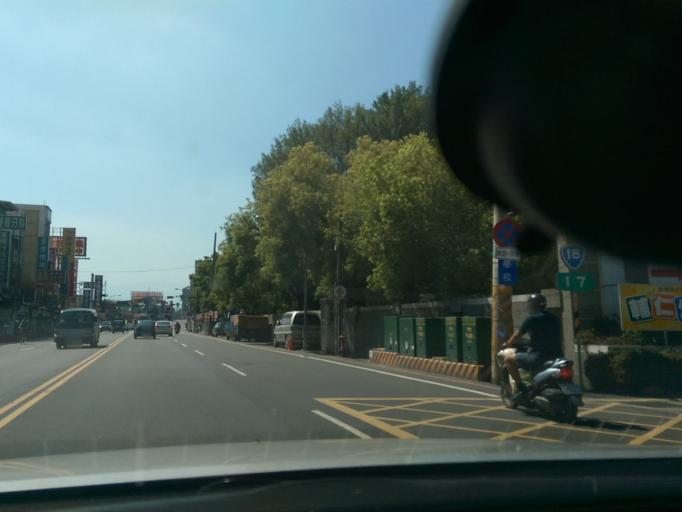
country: TW
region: Taiwan
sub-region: Chiayi
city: Jiayi Shi
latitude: 23.4621
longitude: 120.4564
